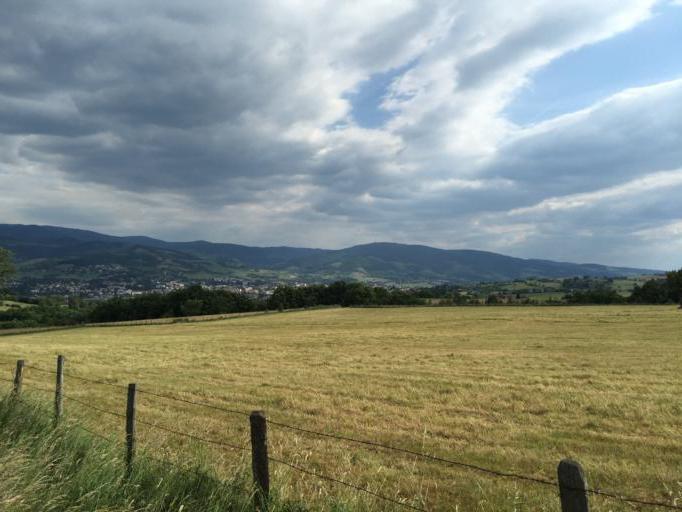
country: FR
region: Rhone-Alpes
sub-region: Departement de la Loire
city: Saint-Chamond
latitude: 45.5026
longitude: 4.5116
